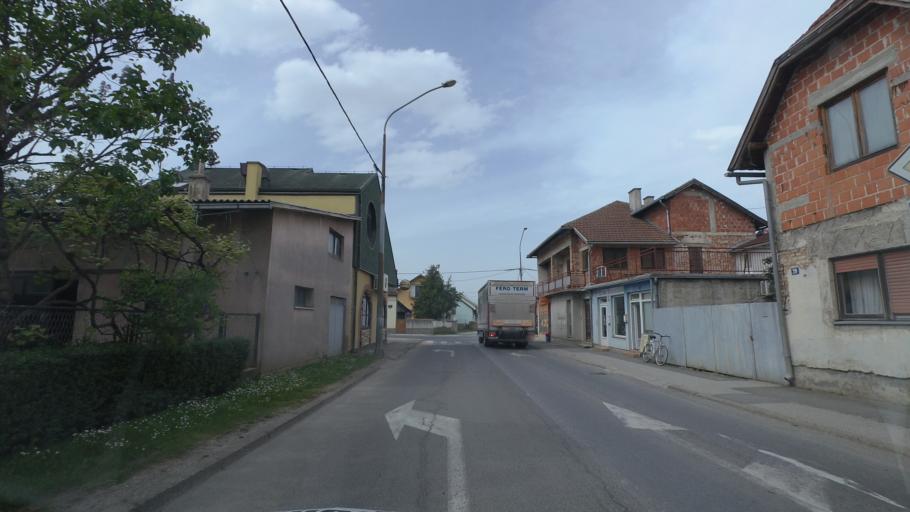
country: HR
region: Sisacko-Moslavacka
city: Petrinja
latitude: 45.4437
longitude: 16.2840
